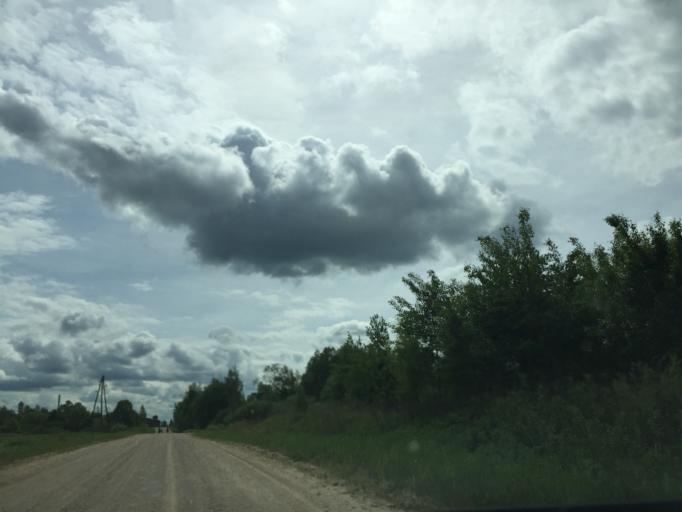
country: LV
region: Dagda
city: Dagda
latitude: 56.0346
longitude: 27.6268
